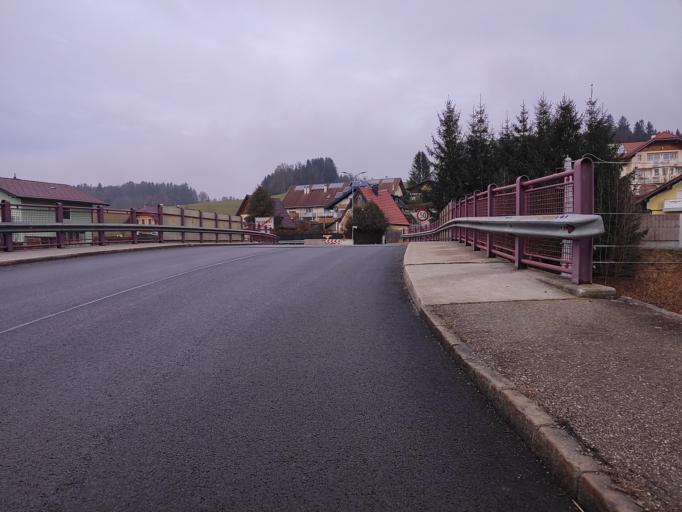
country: AT
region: Salzburg
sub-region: Politischer Bezirk Salzburg-Umgebung
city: Neumarkt am Wallersee
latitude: 47.9511
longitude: 13.2182
